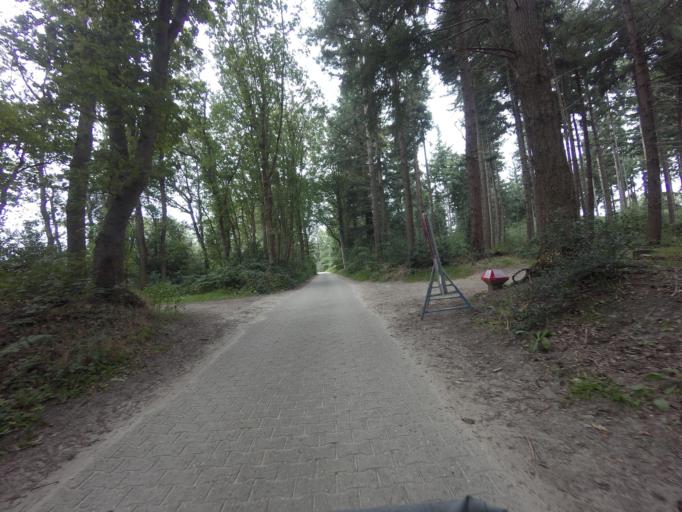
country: NL
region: Overijssel
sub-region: Gemeente Steenwijkerland
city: Tuk
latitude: 52.8180
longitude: 6.1098
